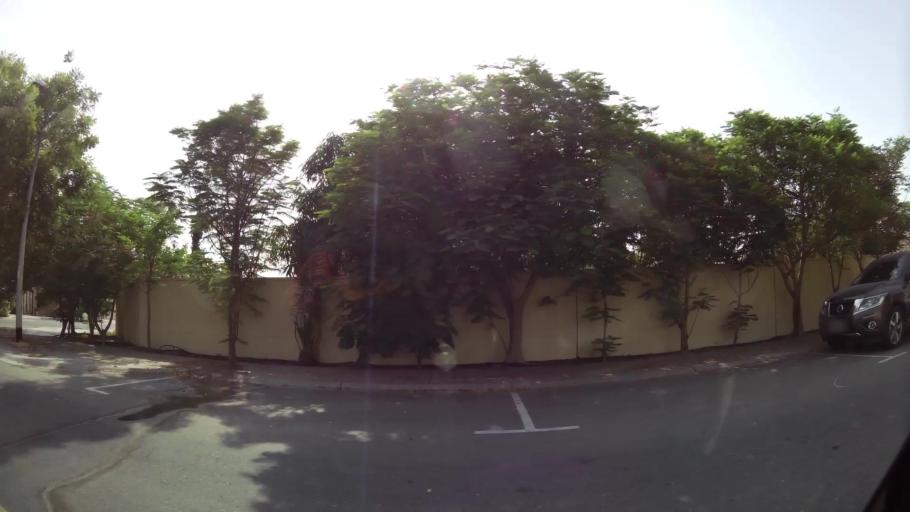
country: AE
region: Ash Shariqah
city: Sharjah
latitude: 25.2675
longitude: 55.4572
